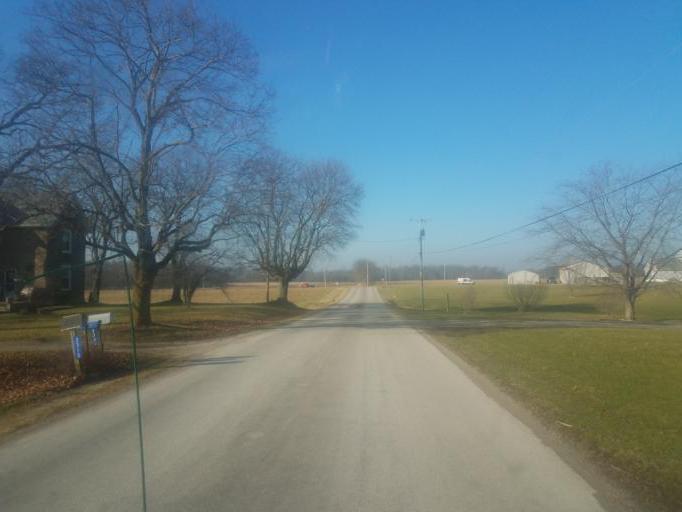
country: US
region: Ohio
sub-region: Crawford County
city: Bucyrus
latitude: 40.8995
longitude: -82.9542
